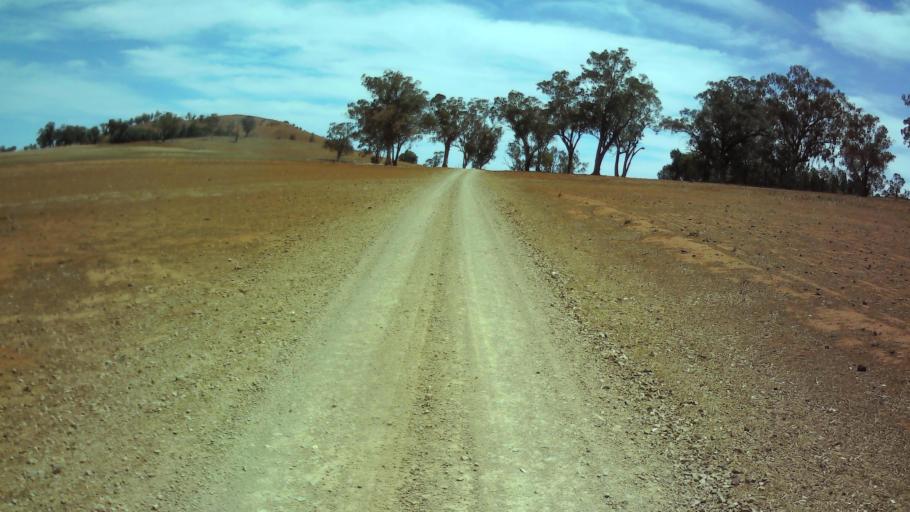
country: AU
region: New South Wales
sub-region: Weddin
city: Grenfell
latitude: -33.7463
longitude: 148.1703
